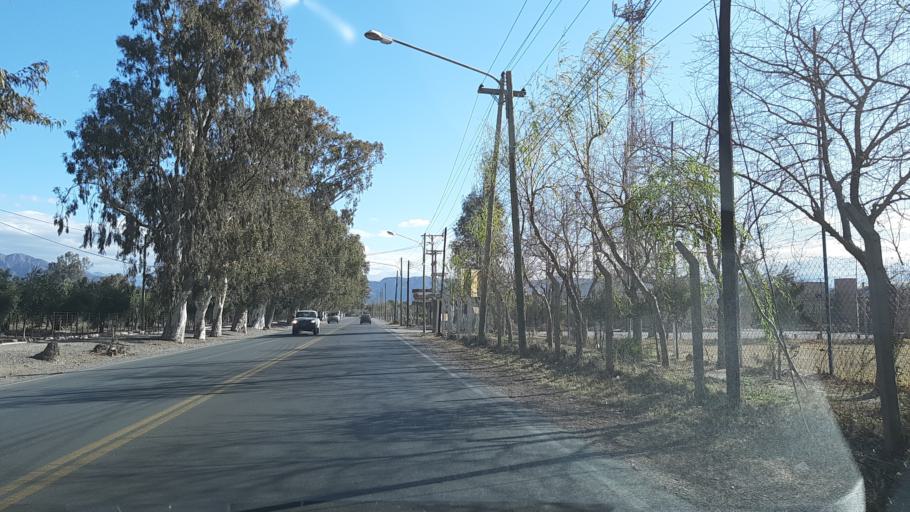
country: AR
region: San Juan
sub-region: Departamento de Rivadavia
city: Rivadavia
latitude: -31.5390
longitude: -68.6074
